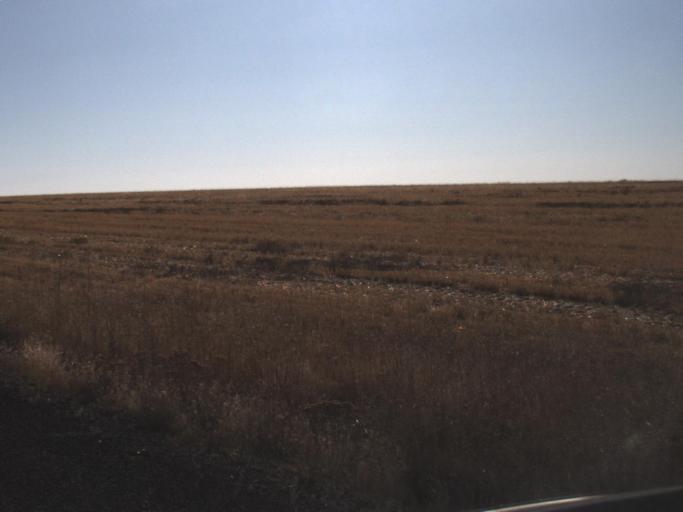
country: US
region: Washington
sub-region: Franklin County
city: Connell
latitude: 46.6202
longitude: -118.6865
